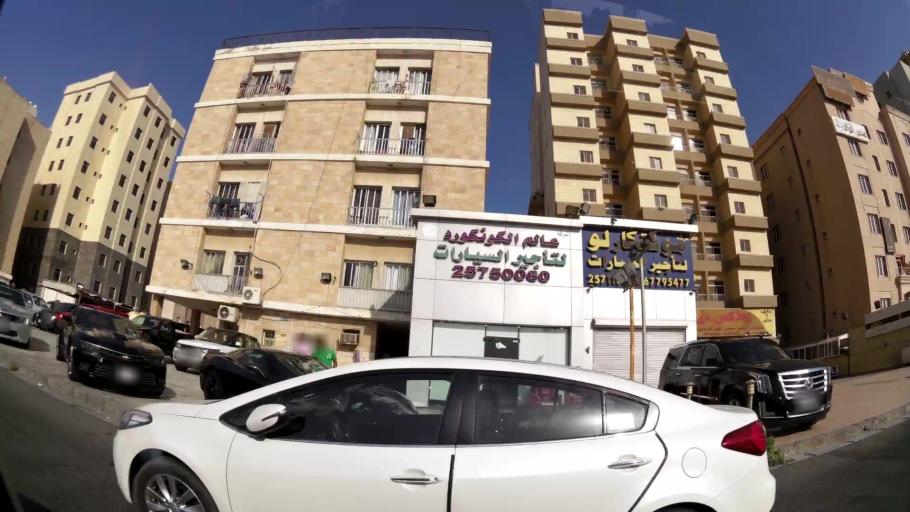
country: KW
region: Muhafazat Hawalli
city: As Salimiyah
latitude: 29.3257
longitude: 48.0853
